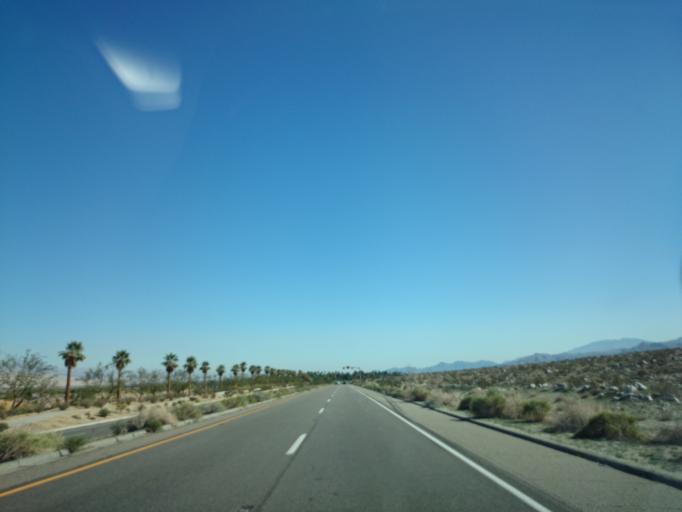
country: US
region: California
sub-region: Riverside County
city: Palm Springs
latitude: 33.8646
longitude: -116.5679
